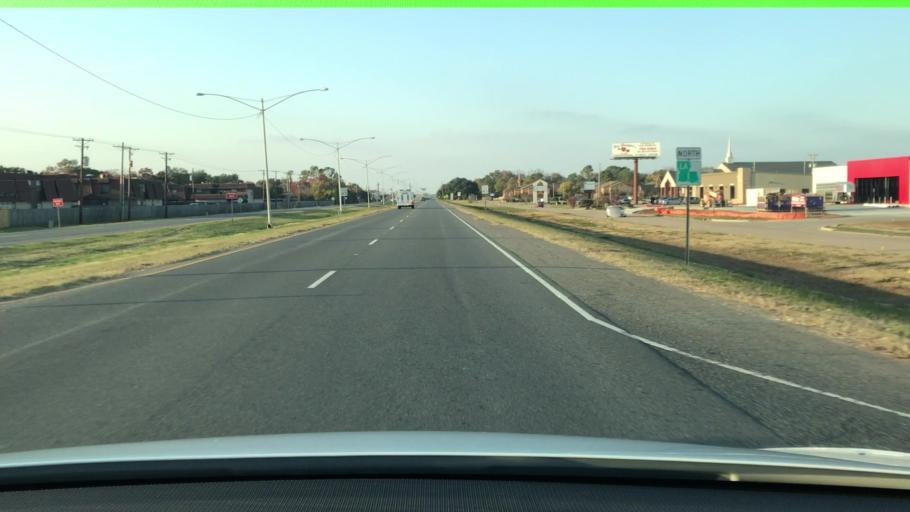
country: US
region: Louisiana
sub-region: Bossier Parish
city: Bossier City
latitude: 32.4130
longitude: -93.7009
